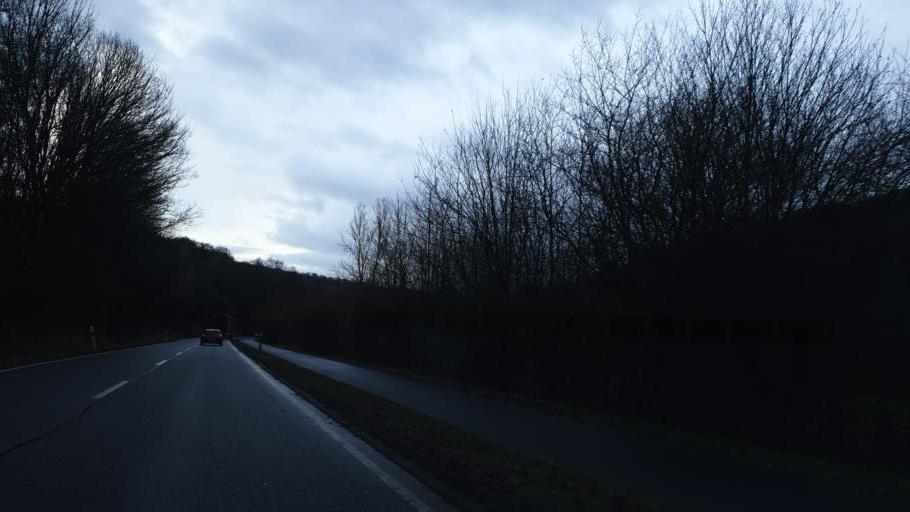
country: DE
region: Hesse
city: Eppstein
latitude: 50.1677
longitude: 8.3754
